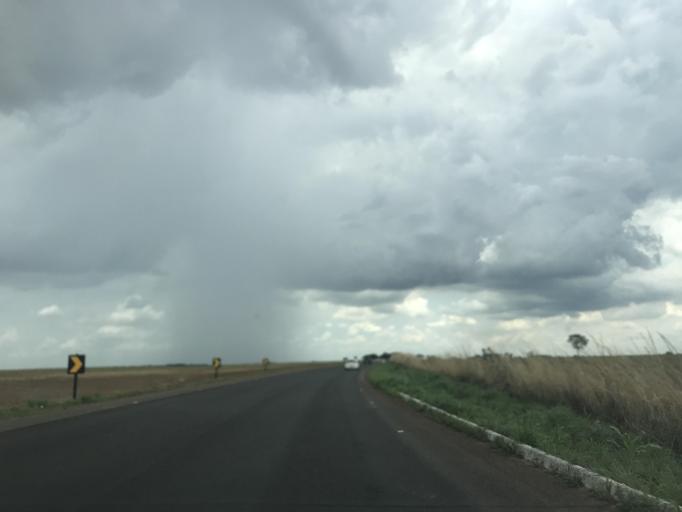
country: BR
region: Goias
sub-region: Vianopolis
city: Vianopolis
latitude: -16.8592
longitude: -48.5413
